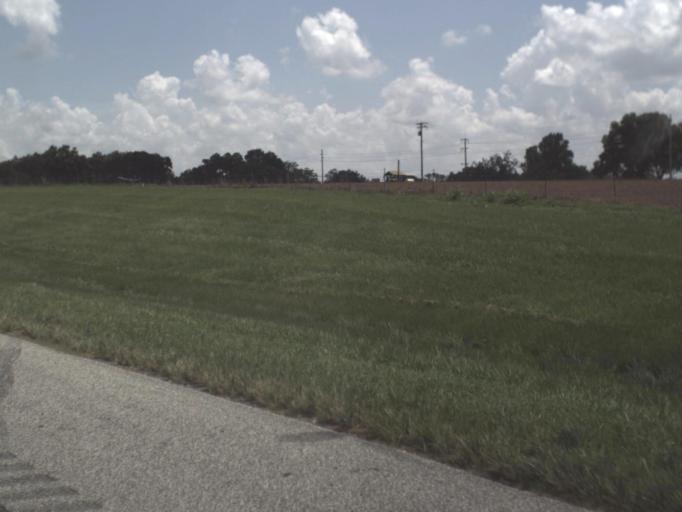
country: US
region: Florida
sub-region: Hillsborough County
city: Dover
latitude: 28.0268
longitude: -82.1944
